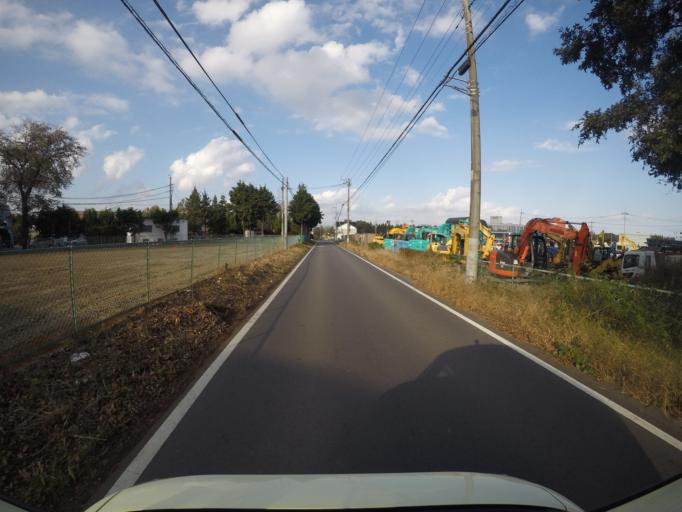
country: JP
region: Ibaraki
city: Naka
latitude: 36.0518
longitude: 140.0837
